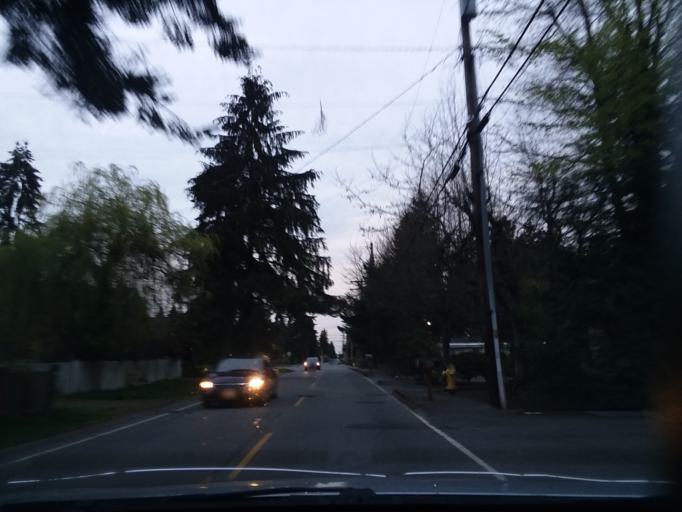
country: US
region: Washington
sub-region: Snohomish County
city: Esperance
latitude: 47.8023
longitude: -122.3410
